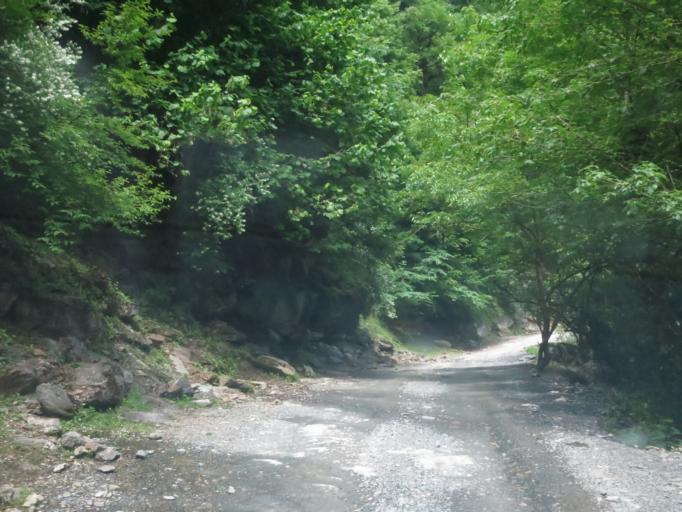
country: GE
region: Kakheti
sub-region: Telavi
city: Telavi
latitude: 42.2109
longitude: 45.4670
